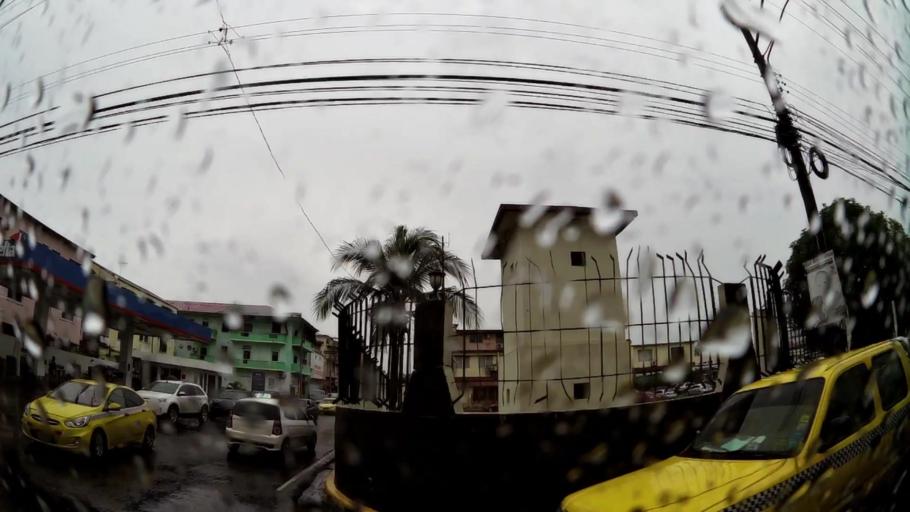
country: PA
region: Colon
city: Colon
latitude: 9.3564
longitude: -79.8991
